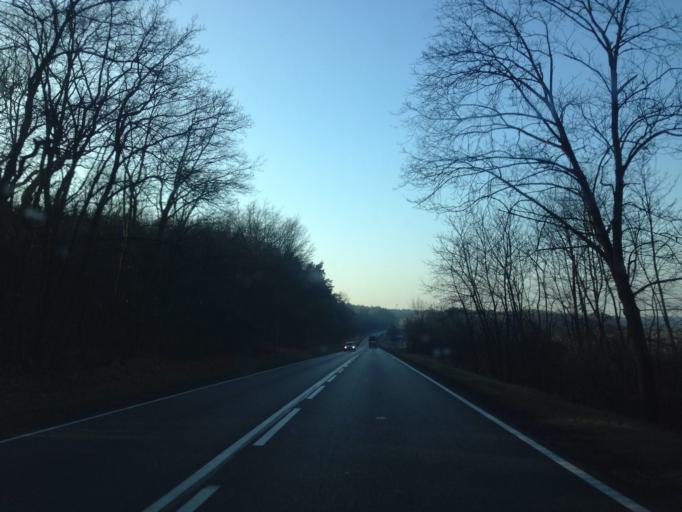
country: PL
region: Kujawsko-Pomorskie
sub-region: Powiat torunski
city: Zlawies Wielka
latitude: 53.0506
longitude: 18.3508
